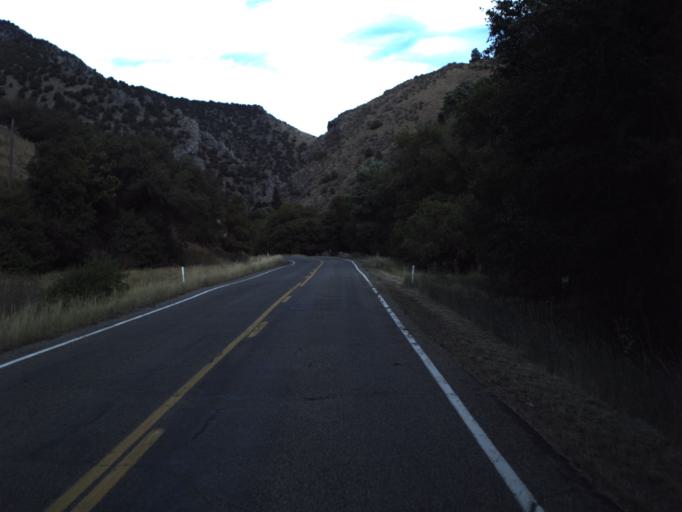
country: US
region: Utah
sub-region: Cache County
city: Millville
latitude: 41.6293
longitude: -111.7147
